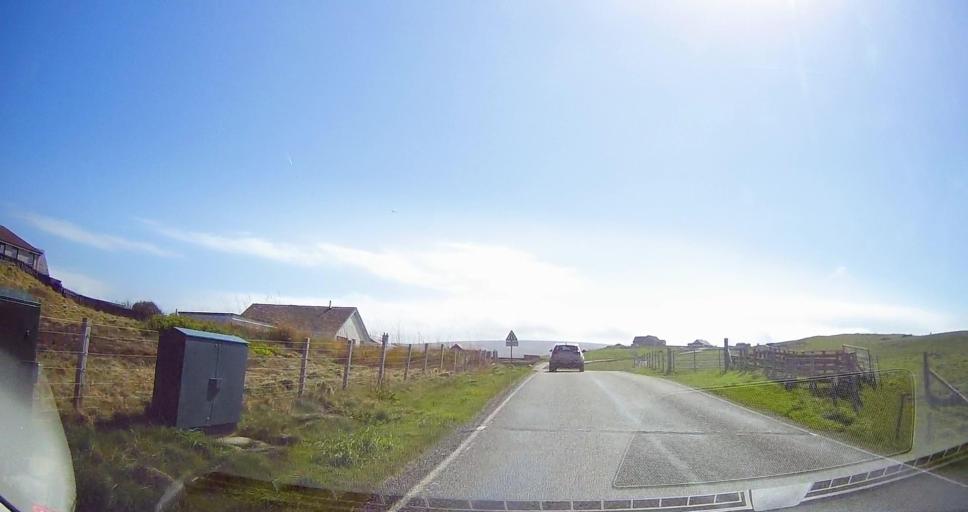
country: GB
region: Scotland
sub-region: Shetland Islands
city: Sandwick
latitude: 60.1030
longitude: -1.3255
